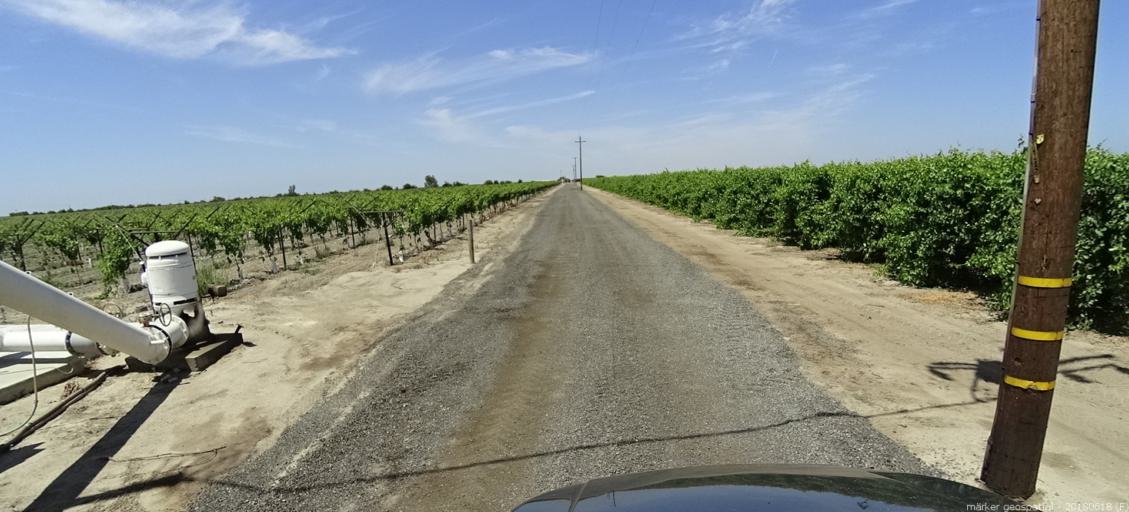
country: US
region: California
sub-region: Madera County
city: Parkwood
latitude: 36.8875
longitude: -120.1331
